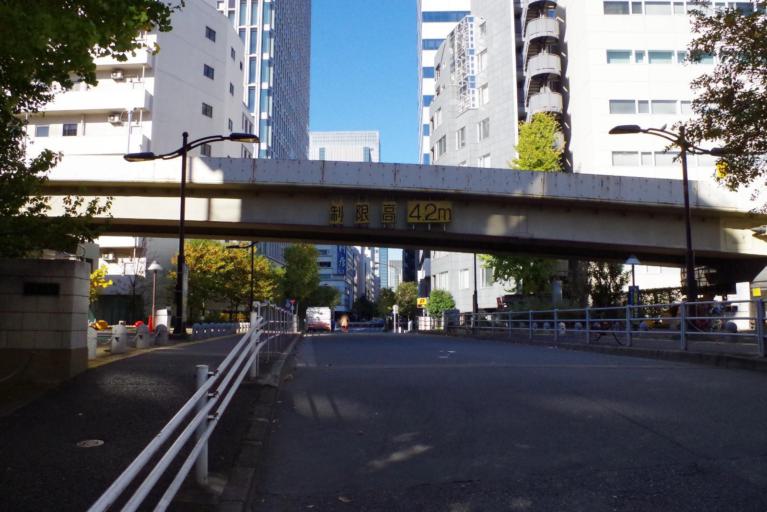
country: JP
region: Tokyo
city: Tokyo
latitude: 35.6764
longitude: 139.7743
